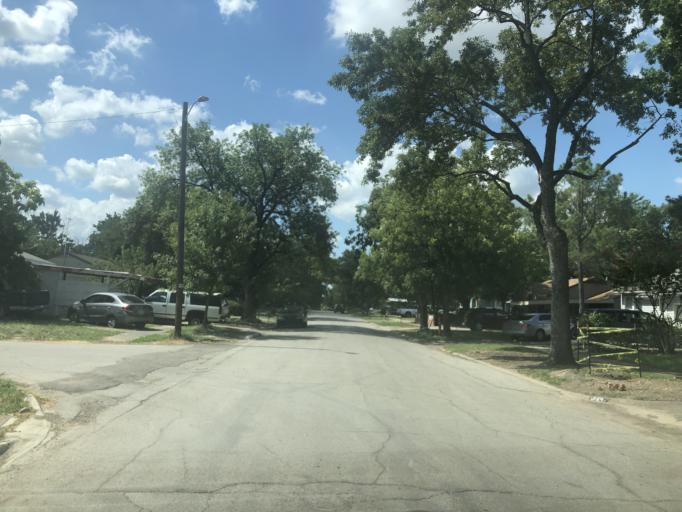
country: US
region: Texas
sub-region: Dallas County
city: Grand Prairie
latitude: 32.7333
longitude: -97.0091
